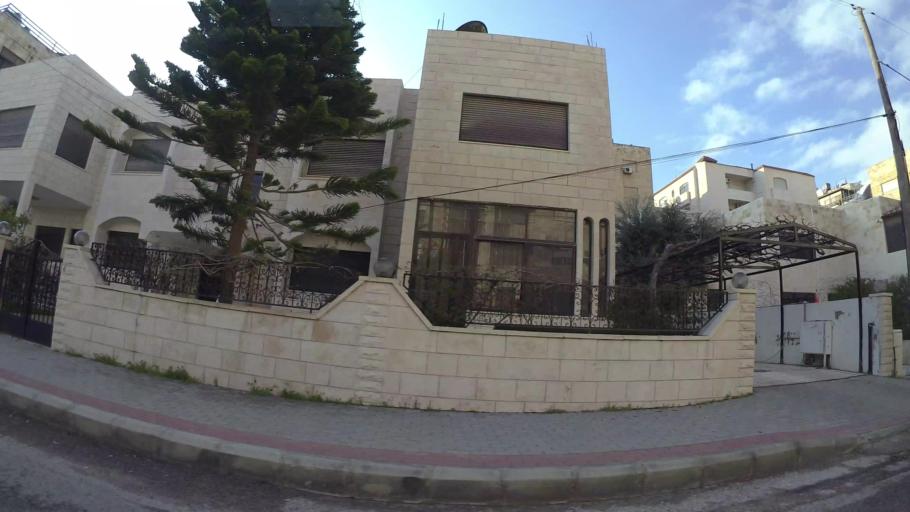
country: JO
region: Amman
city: Al Jubayhah
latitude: 31.9810
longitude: 35.8707
